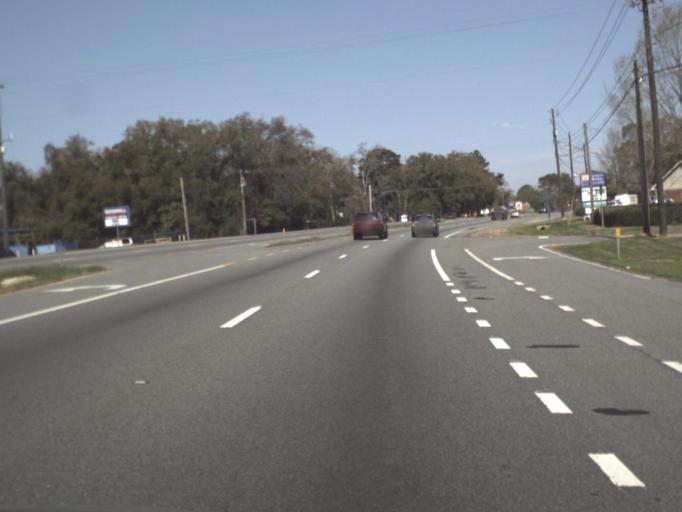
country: US
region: Florida
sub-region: Leon County
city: Tallahassee
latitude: 30.4900
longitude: -84.3223
